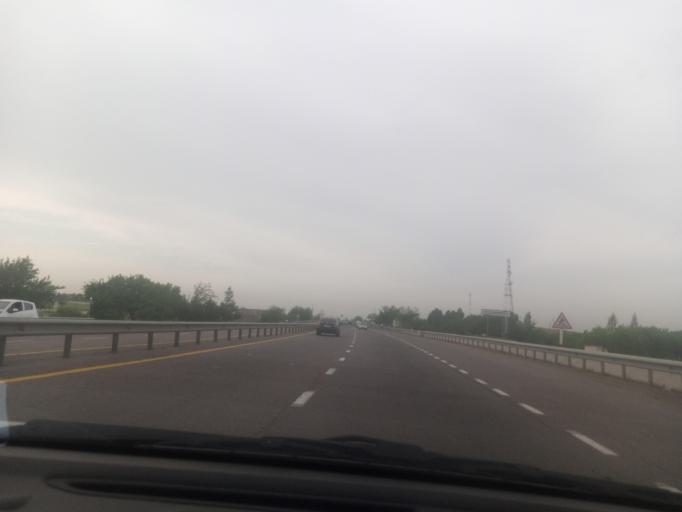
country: UZ
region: Toshkent
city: Tuytepa
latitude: 41.1261
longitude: 69.4379
